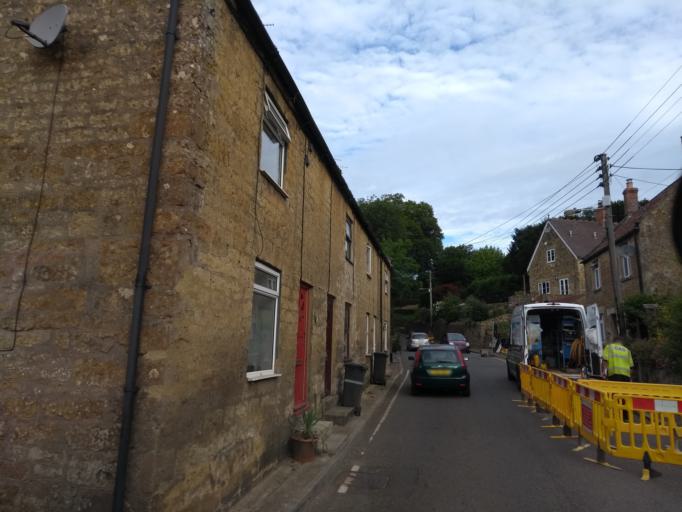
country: GB
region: England
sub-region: Somerset
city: Crewkerne
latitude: 50.8708
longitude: -2.7758
